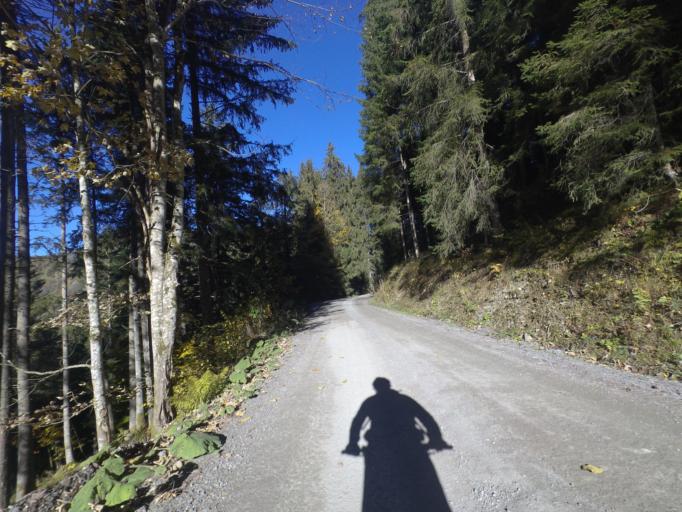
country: AT
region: Salzburg
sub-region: Politischer Bezirk Sankt Johann im Pongau
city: Sankt Johann im Pongau
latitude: 47.3260
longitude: 13.2324
